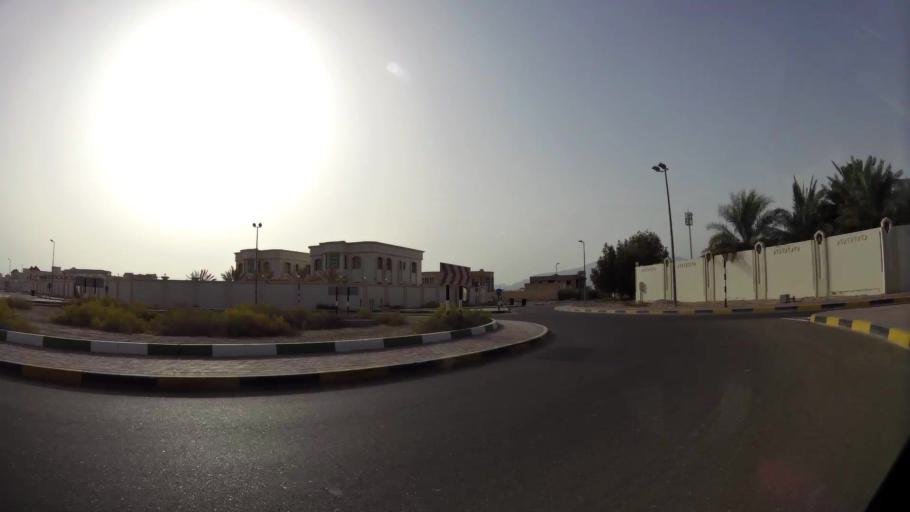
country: AE
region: Abu Dhabi
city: Al Ain
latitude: 24.1289
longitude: 55.6975
